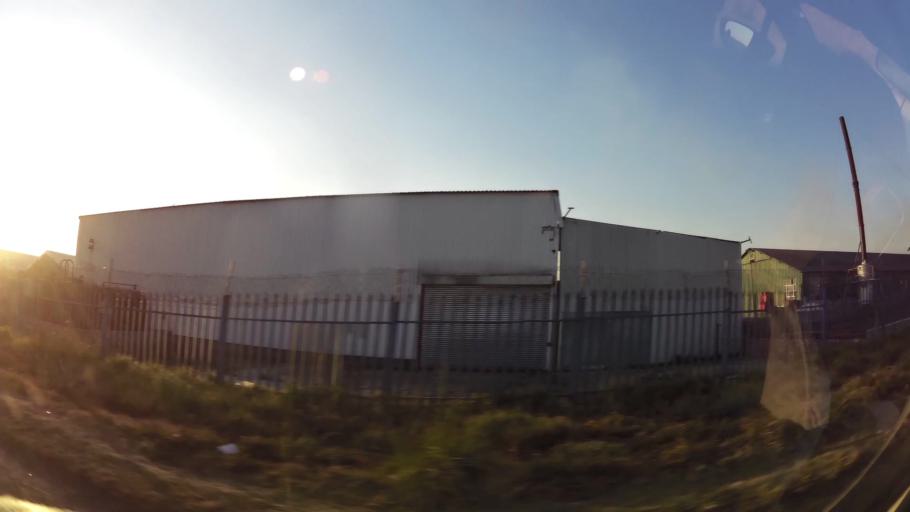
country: ZA
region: Gauteng
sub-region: West Rand District Municipality
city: Randfontein
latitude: -26.2020
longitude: 27.6810
